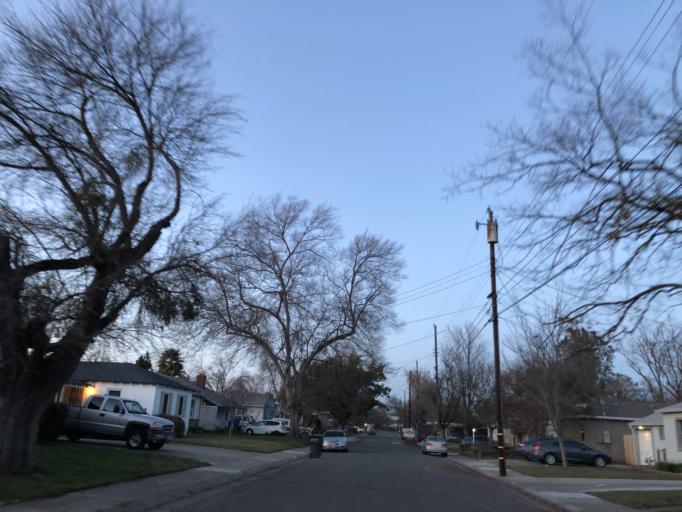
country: US
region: California
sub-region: Sacramento County
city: Parkway
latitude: 38.5479
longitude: -121.4379
